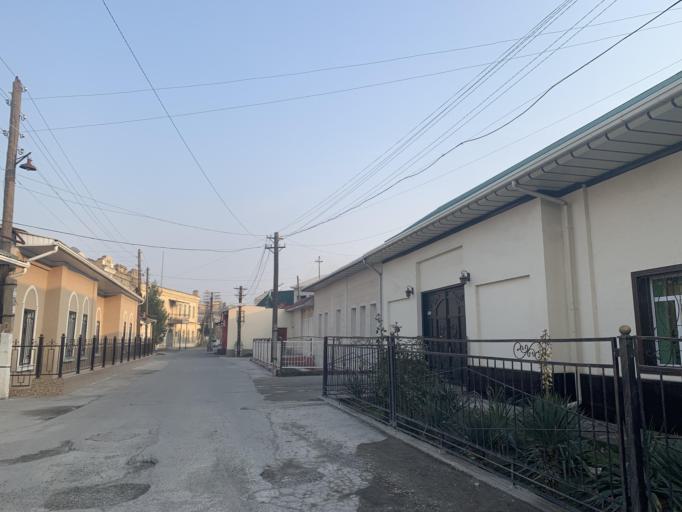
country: UZ
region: Fergana
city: Qo`qon
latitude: 40.5376
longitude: 70.9308
